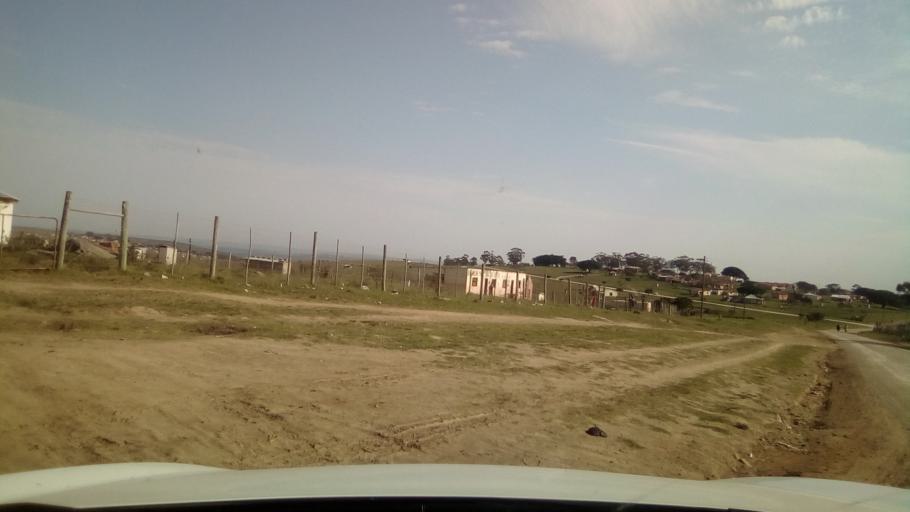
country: ZA
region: Eastern Cape
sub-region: Buffalo City Metropolitan Municipality
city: Bhisho
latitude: -32.9864
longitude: 27.2672
